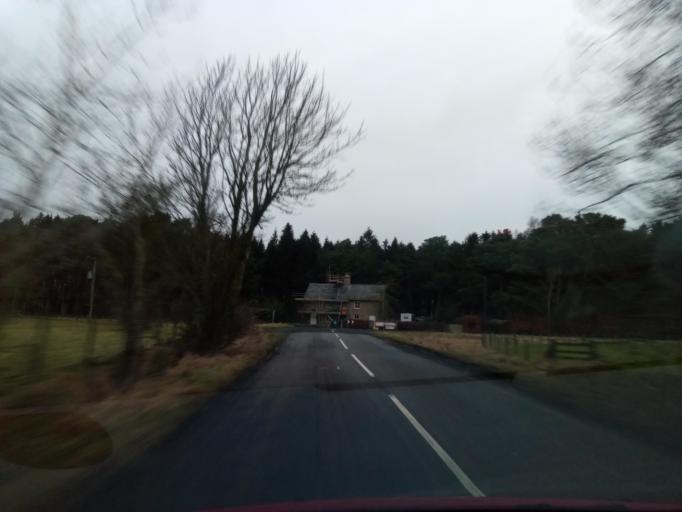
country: GB
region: England
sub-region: Northumberland
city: Rothley
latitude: 55.1982
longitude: -1.9727
